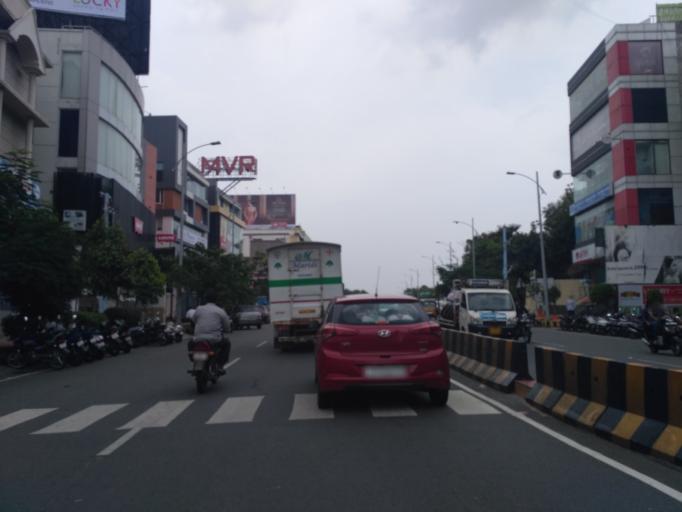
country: IN
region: Andhra Pradesh
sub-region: Vishakhapatnam
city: Yarada
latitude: 17.7249
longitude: 83.3142
